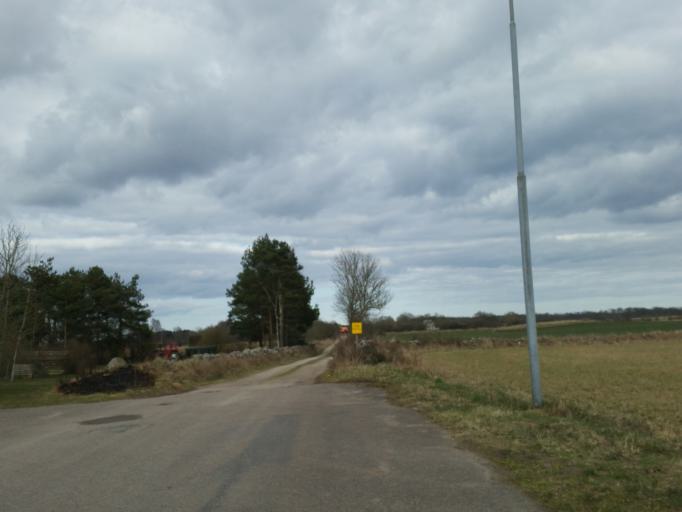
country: SE
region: Kalmar
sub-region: Morbylanga Kommun
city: Sodra Sandby
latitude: 56.6057
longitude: 16.6472
